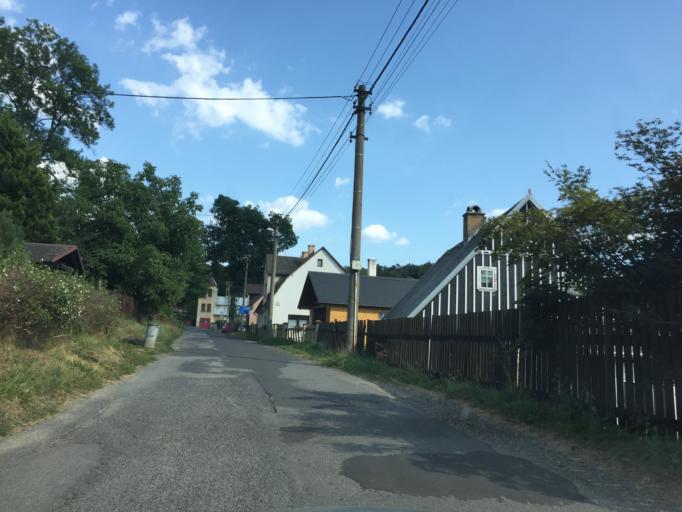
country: CZ
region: Liberecky
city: Mala Skala
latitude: 50.6755
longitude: 15.1673
